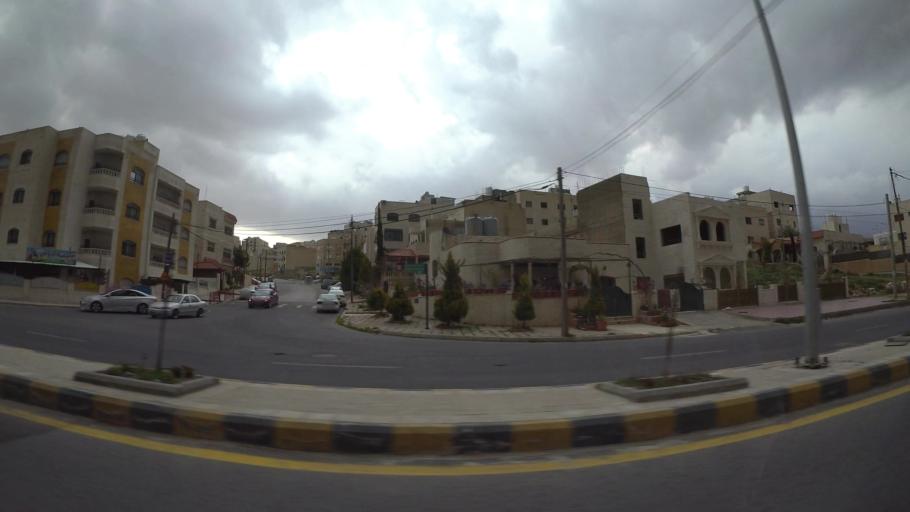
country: JO
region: Amman
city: Amman
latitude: 32.0099
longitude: 35.9598
